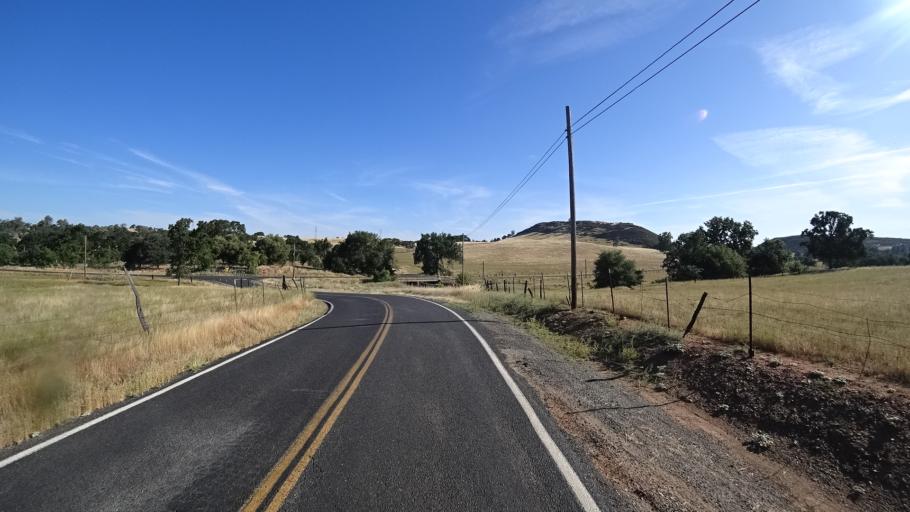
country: US
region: California
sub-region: Calaveras County
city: Valley Springs
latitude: 38.1922
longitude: -120.8060
